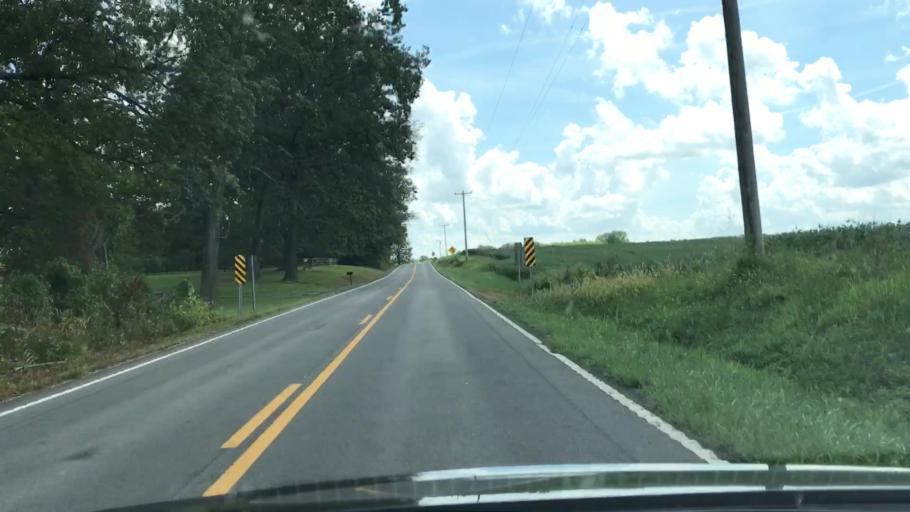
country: US
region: Tennessee
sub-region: Robertson County
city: Springfield
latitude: 36.5725
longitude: -86.8648
